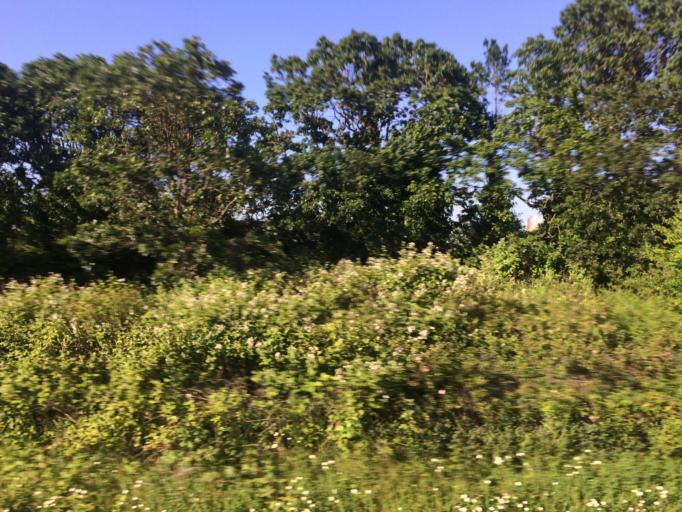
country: CA
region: British Columbia
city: Victoria
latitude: 48.4609
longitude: -123.4094
